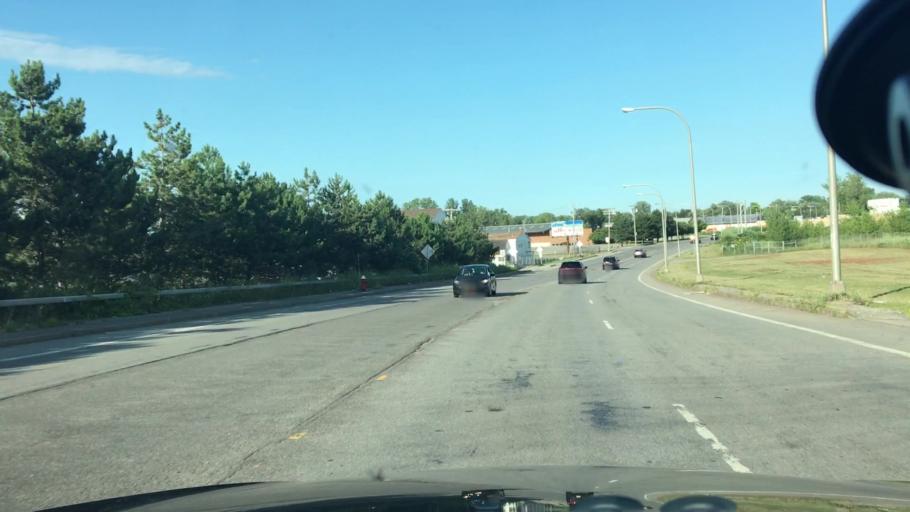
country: US
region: New York
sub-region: Erie County
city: Lackawanna
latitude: 42.8464
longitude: -78.8397
